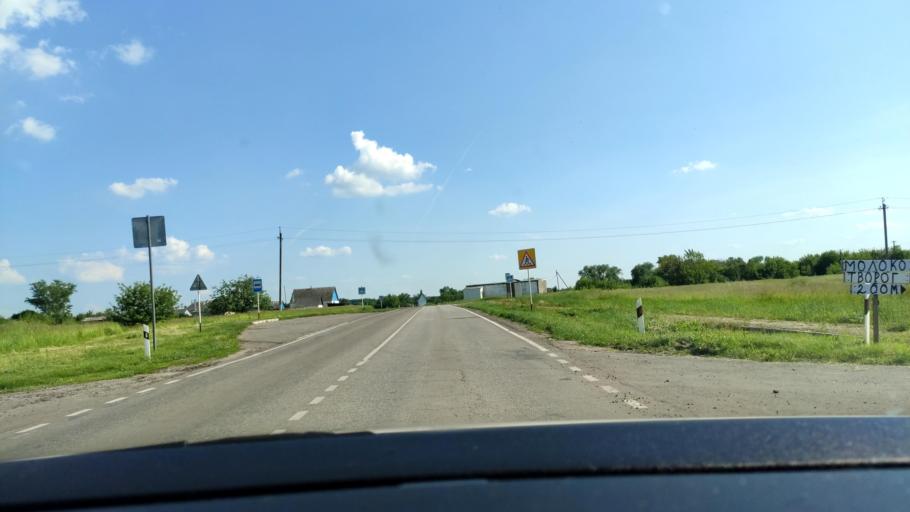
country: RU
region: Voronezj
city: Verkhnyaya Khava
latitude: 51.6763
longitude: 39.9416
